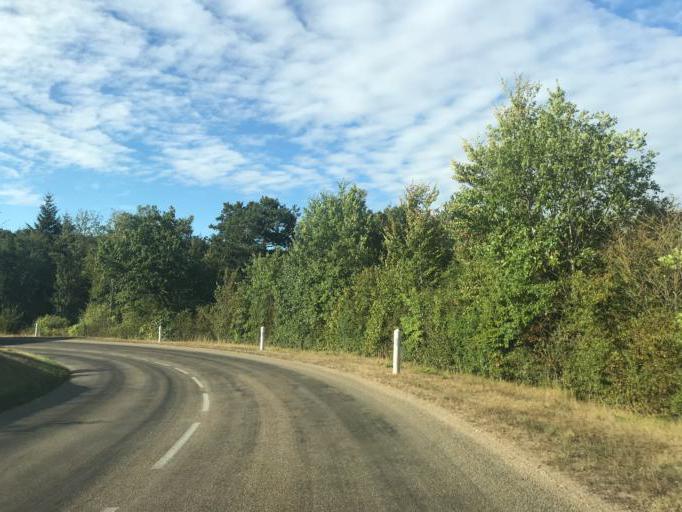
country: FR
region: Bourgogne
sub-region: Departement de l'Yonne
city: Fontenailles
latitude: 47.5964
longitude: 3.4746
